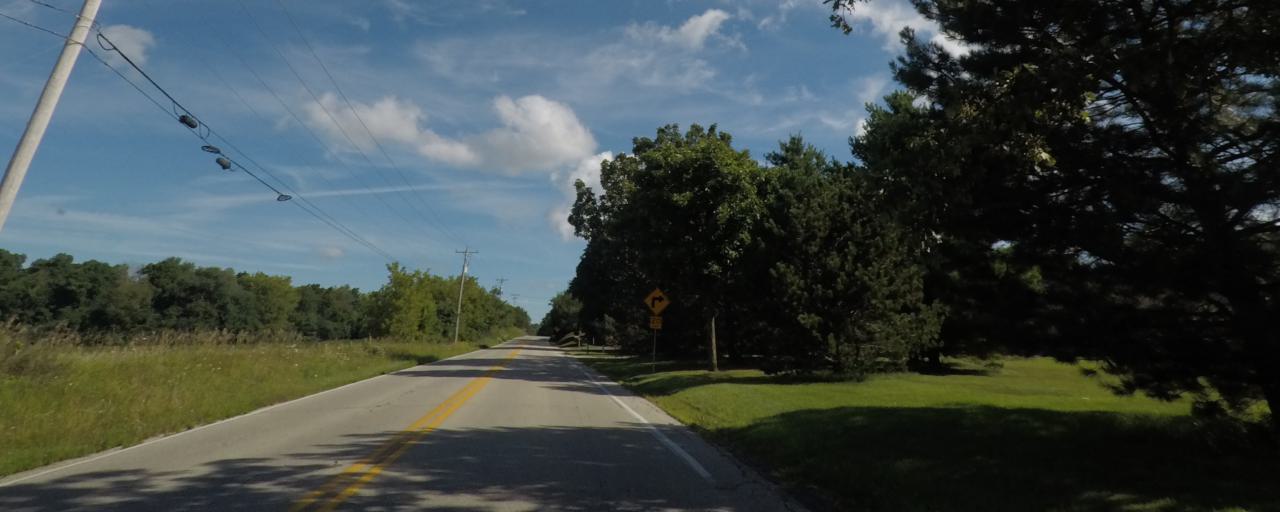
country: US
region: Wisconsin
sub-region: Waukesha County
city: Oconomowoc
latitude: 43.0786
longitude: -88.5400
